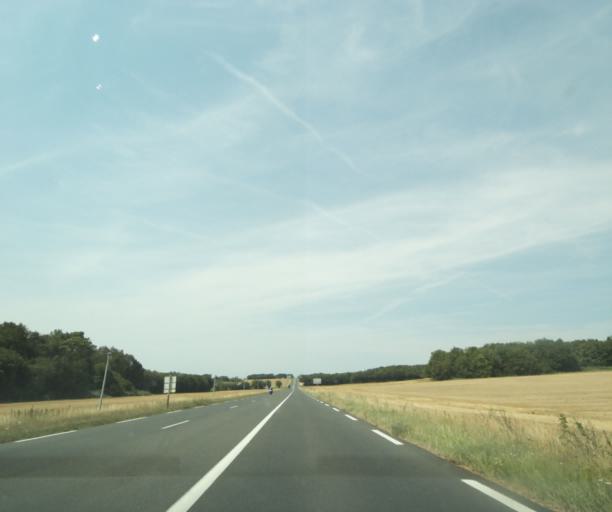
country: FR
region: Centre
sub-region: Departement d'Indre-et-Loire
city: Sainte-Maure-de-Touraine
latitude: 47.0792
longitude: 0.6127
